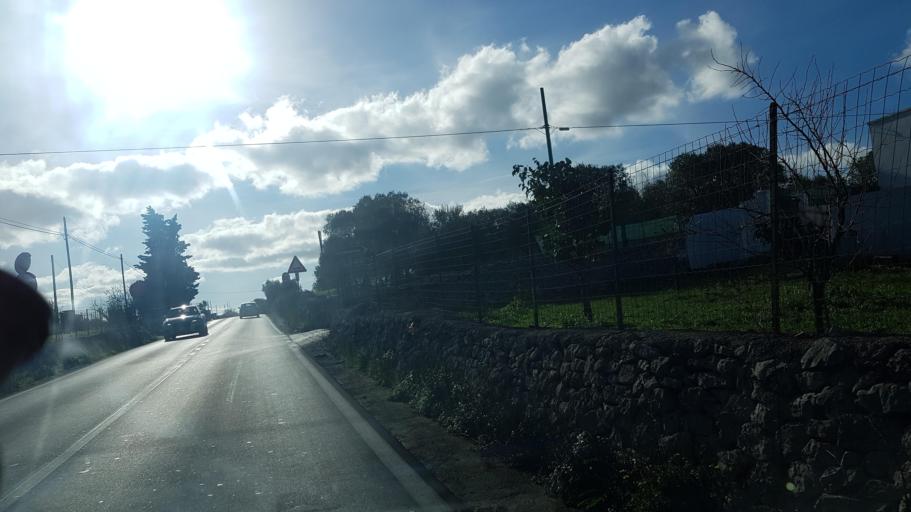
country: IT
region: Apulia
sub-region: Provincia di Brindisi
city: Ostuni
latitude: 40.7122
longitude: 17.5698
